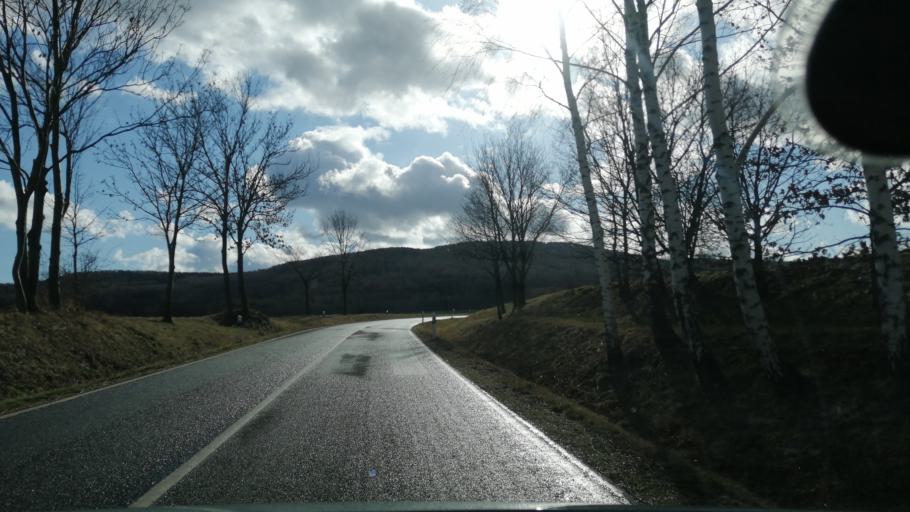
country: DE
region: Saxony
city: Cunewalde
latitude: 51.1397
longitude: 14.5347
